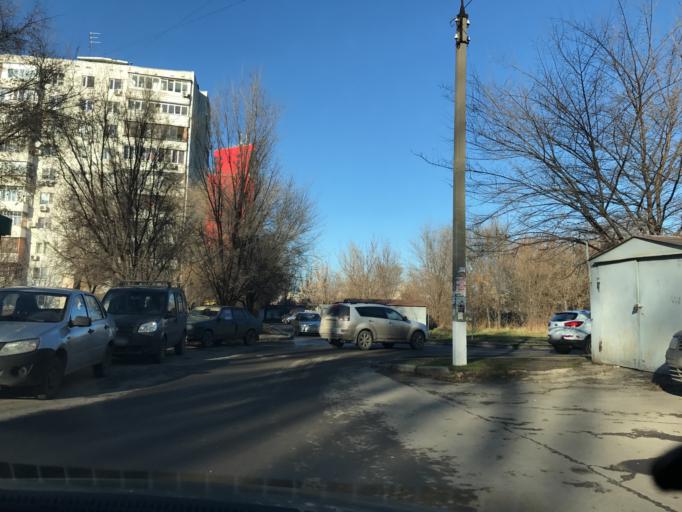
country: RU
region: Rostov
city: Rostov-na-Donu
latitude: 47.2138
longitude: 39.6227
